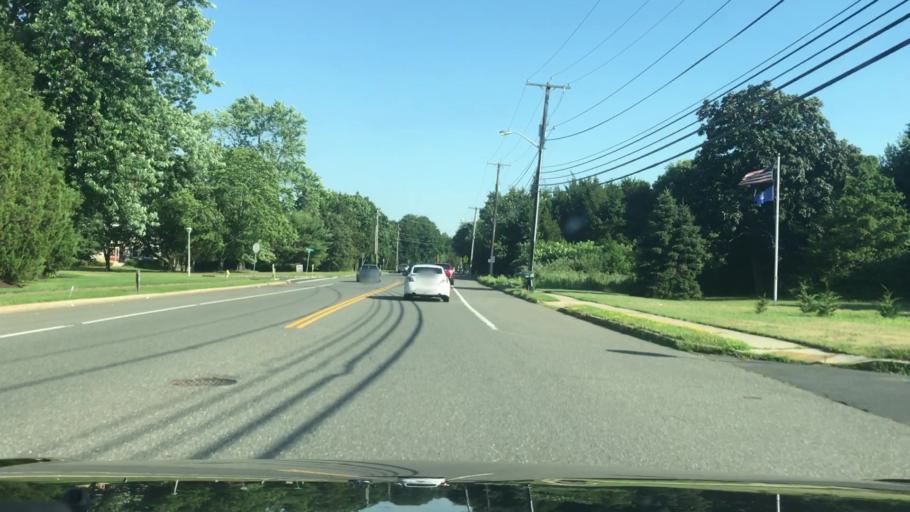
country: US
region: New Jersey
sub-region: Ocean County
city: Silver Ridge
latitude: 39.9972
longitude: -74.1978
